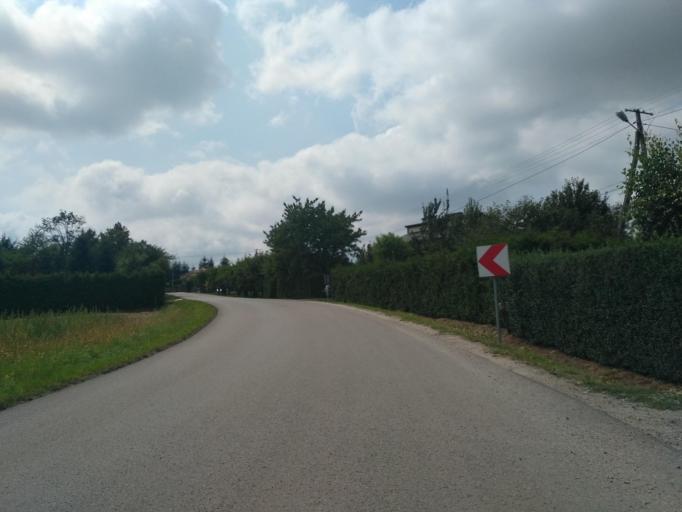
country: PL
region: Subcarpathian Voivodeship
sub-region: Powiat lancucki
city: Kraczkowa
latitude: 50.0156
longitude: 22.1617
